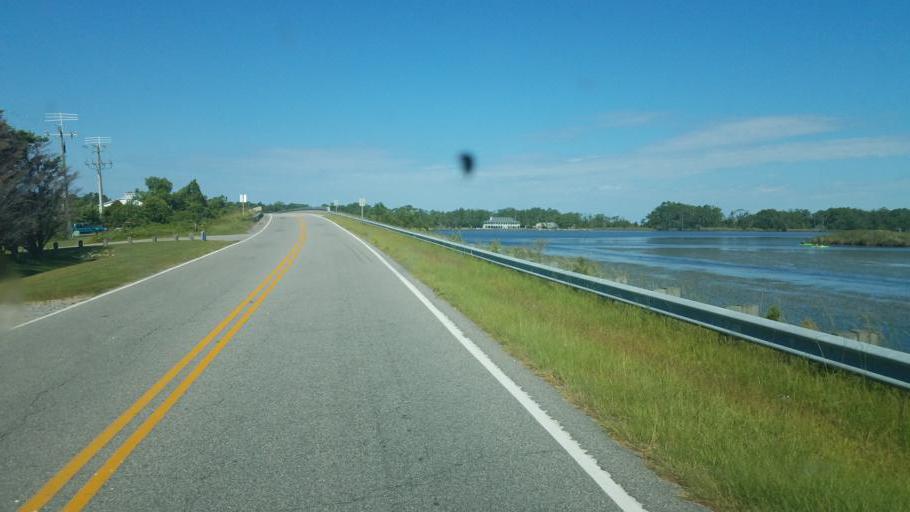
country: US
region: North Carolina
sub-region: Dare County
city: Kill Devil Hills
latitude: 36.0154
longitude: -75.6847
